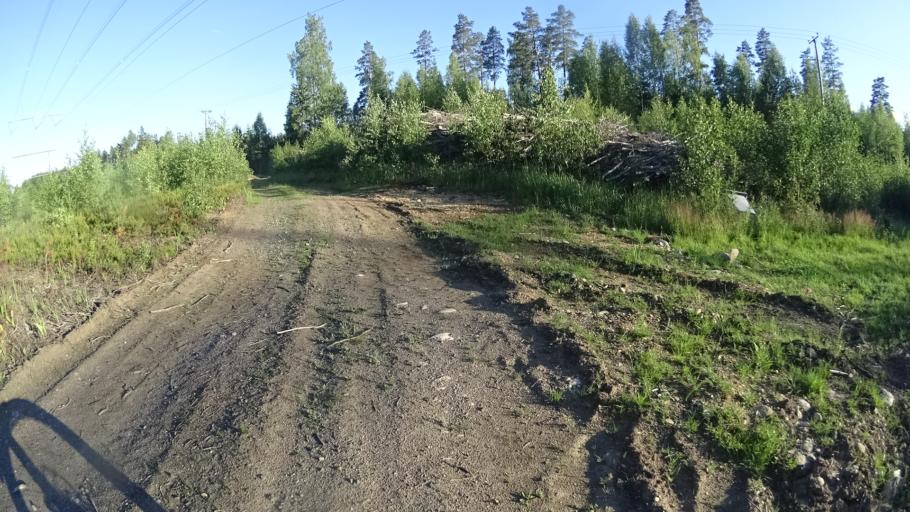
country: FI
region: Uusimaa
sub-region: Helsinki
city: Karkkila
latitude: 60.5944
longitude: 24.1046
